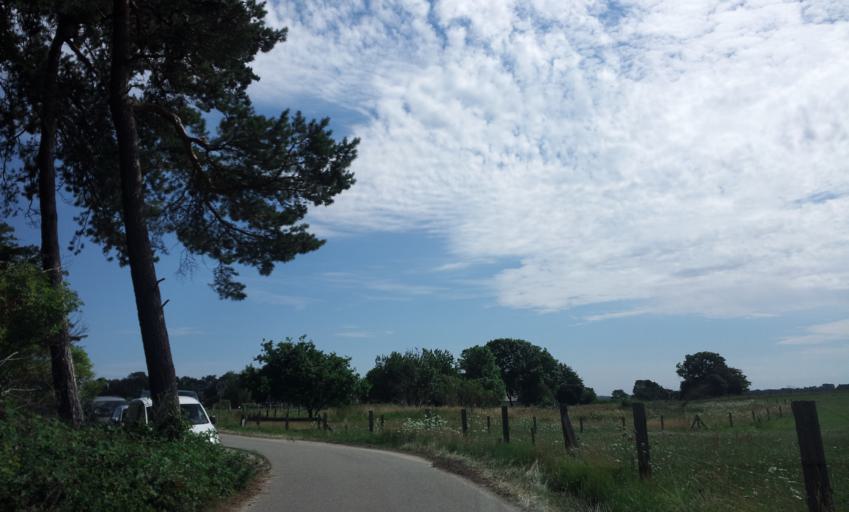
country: DE
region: Mecklenburg-Vorpommern
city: Altenkirchen
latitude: 54.6671
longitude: 13.3051
